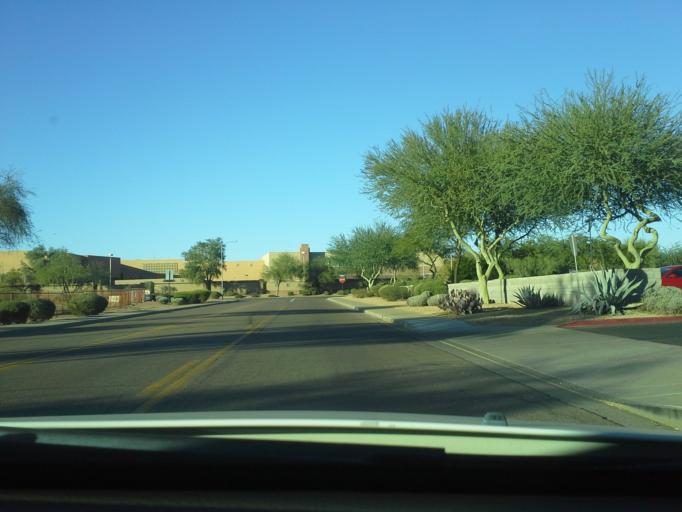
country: US
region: Arizona
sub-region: Maricopa County
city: Paradise Valley
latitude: 33.6320
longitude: -111.9219
